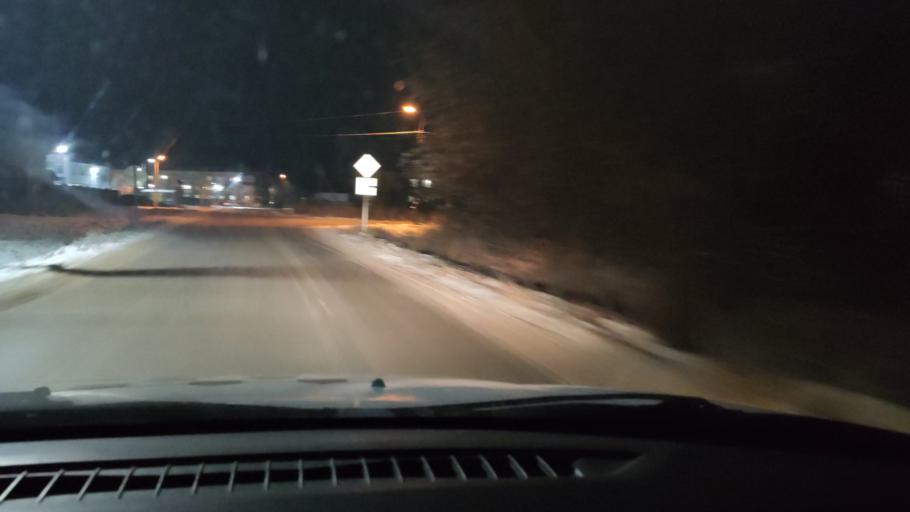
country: RU
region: Perm
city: Ferma
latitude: 57.8957
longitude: 56.3256
